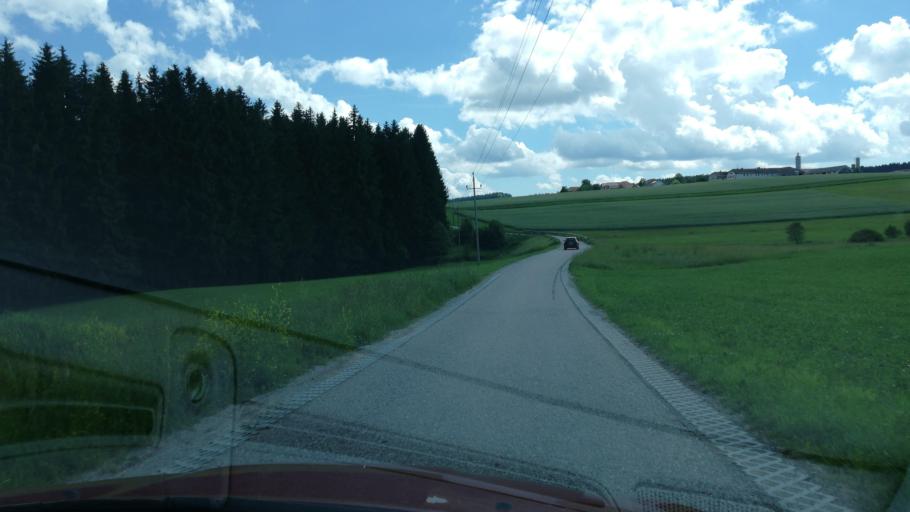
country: AT
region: Upper Austria
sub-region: Politischer Bezirk Urfahr-Umgebung
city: Sonnberg im Muehlkreis
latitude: 48.4604
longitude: 14.3277
